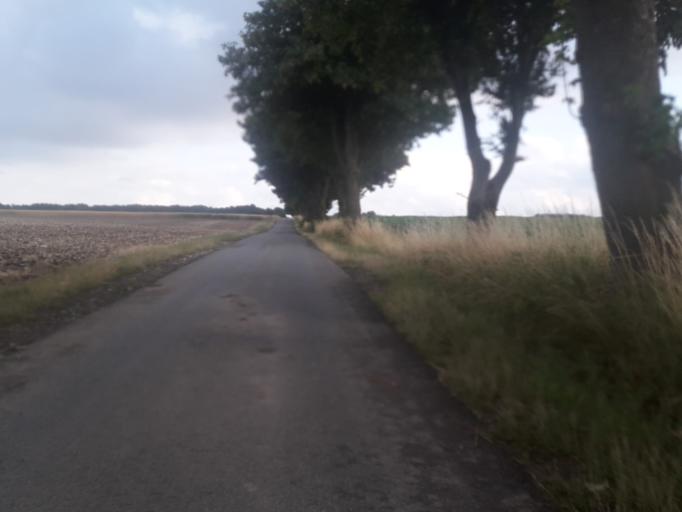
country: DE
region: North Rhine-Westphalia
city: Bad Lippspringe
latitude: 51.7248
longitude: 8.8244
